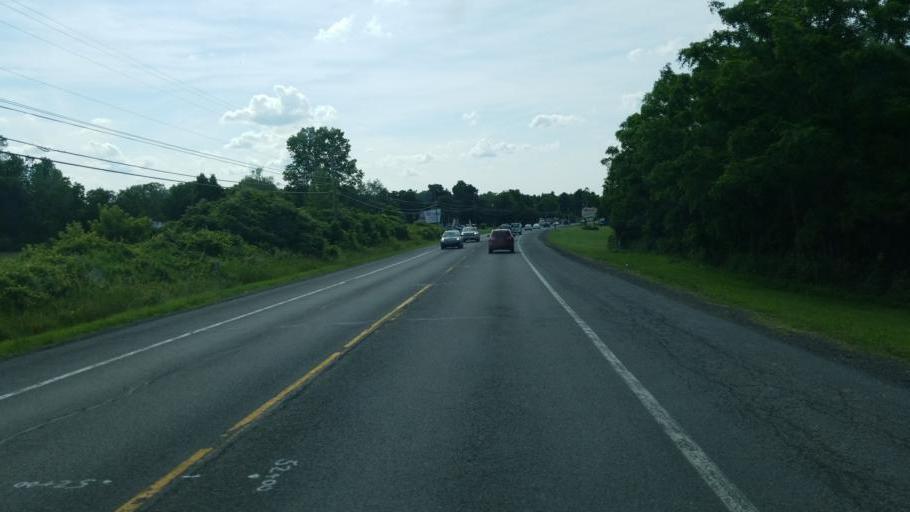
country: US
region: New York
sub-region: Ontario County
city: Canandaigua
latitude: 42.8666
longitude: -77.2267
